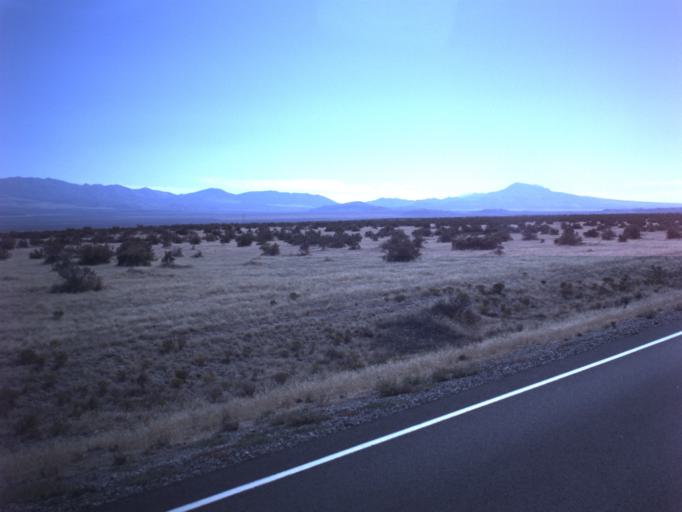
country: US
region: Utah
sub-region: Tooele County
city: Grantsville
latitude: 40.2841
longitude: -112.7420
